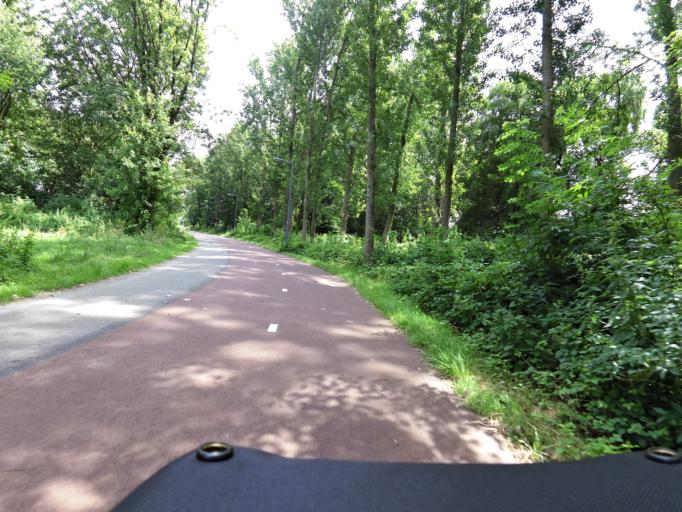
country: NL
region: South Holland
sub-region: Gemeente Vlaardingen
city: Vlaardingen
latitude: 51.8742
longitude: 4.3649
